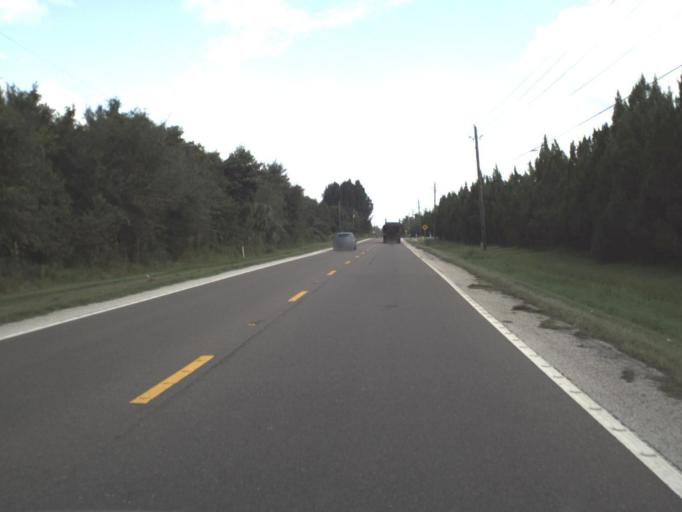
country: US
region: Florida
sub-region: Hardee County
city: Zolfo Springs
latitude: 27.3639
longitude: -81.7991
